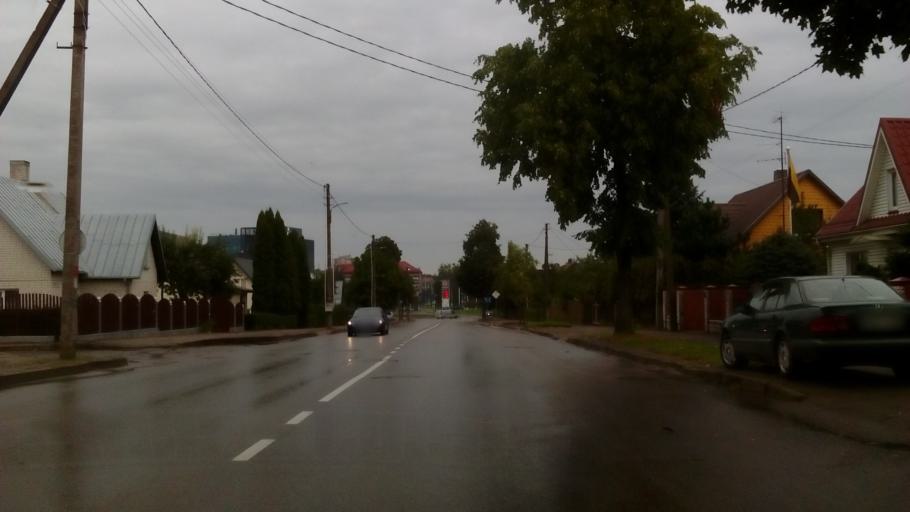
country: LT
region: Alytaus apskritis
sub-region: Alytus
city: Alytus
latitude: 54.3926
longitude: 24.0391
